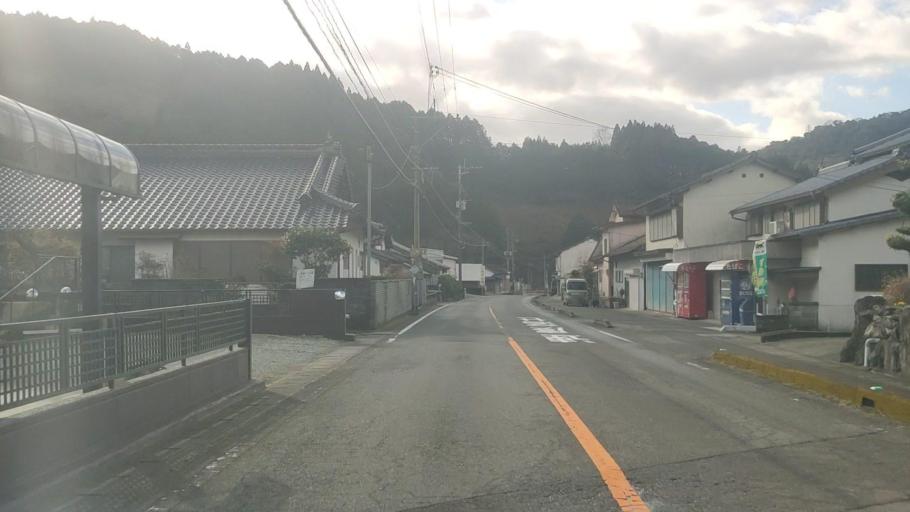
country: JP
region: Kumamoto
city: Hitoyoshi
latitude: 32.3055
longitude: 130.8476
